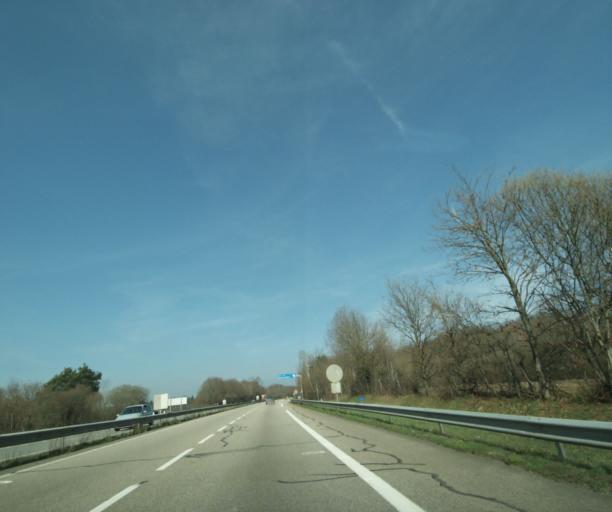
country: FR
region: Limousin
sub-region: Departement de la Haute-Vienne
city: Rilhac-Rancon
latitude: 45.9054
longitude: 1.2918
